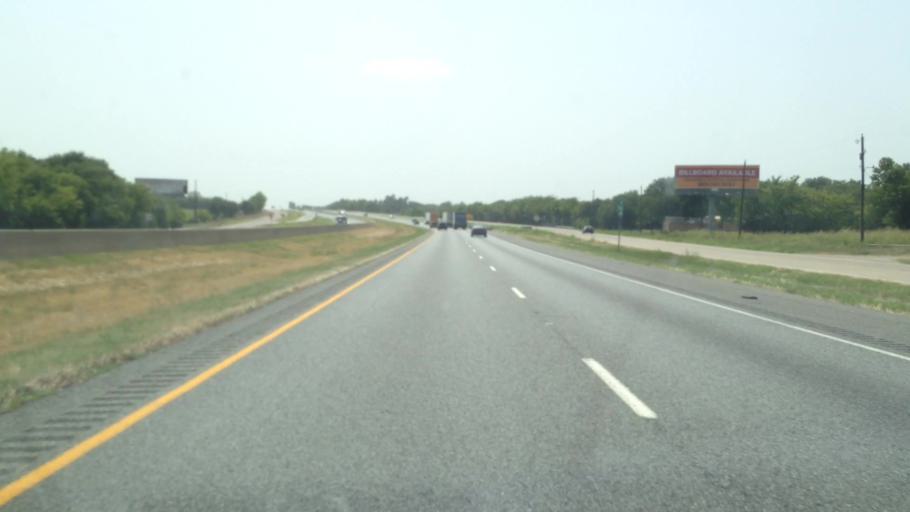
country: US
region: Texas
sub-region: Hunt County
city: Commerce
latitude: 33.1321
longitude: -95.9484
